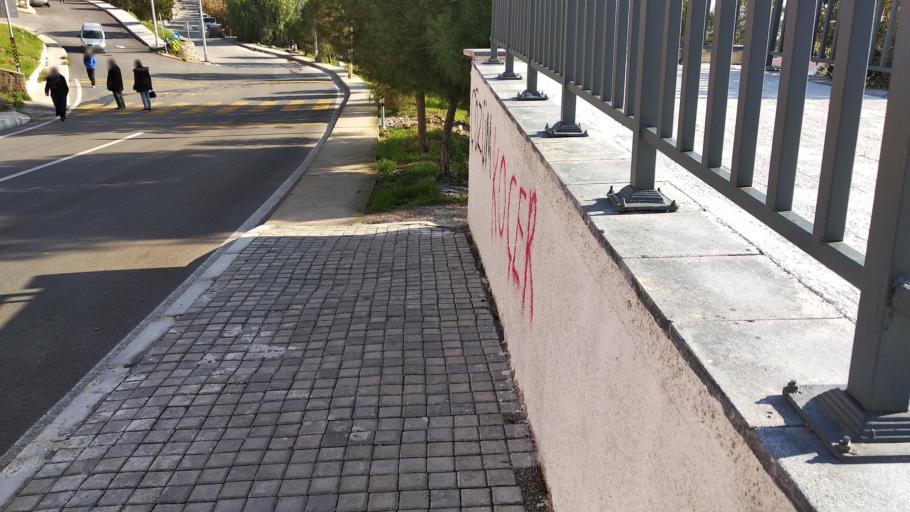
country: TR
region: Izmir
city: Karsiyaka
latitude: 38.4969
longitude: 27.0802
